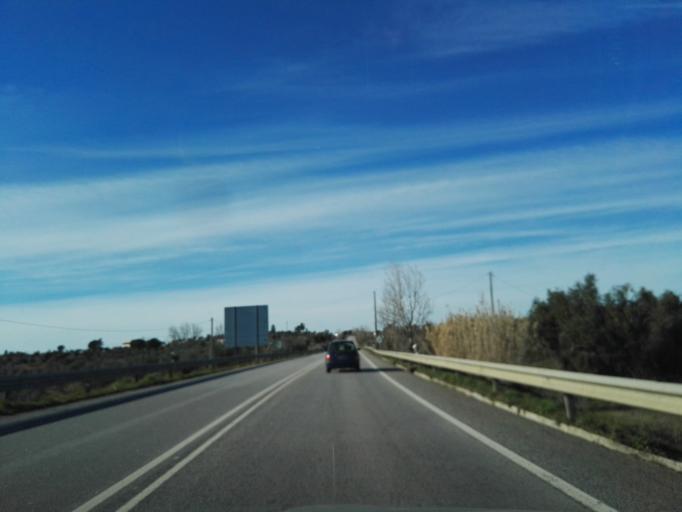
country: PT
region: Santarem
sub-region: Abrantes
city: Alferrarede
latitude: 39.4772
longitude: -8.0837
